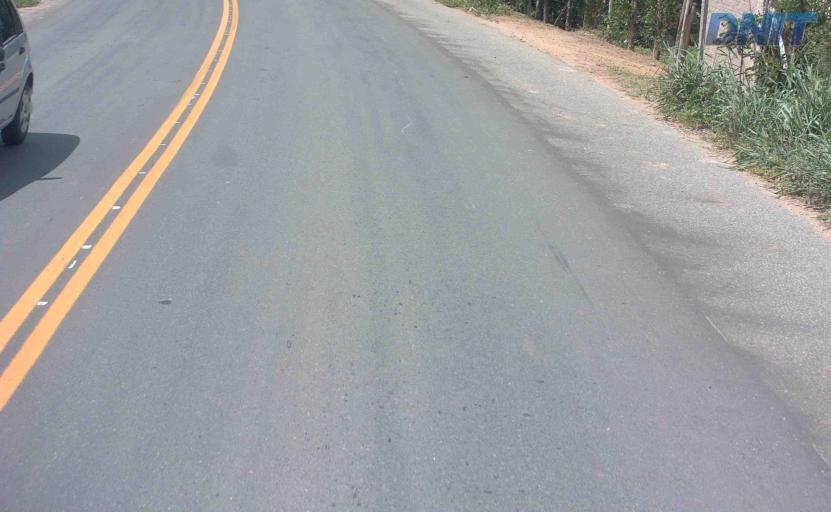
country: BR
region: Minas Gerais
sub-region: Governador Valadares
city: Governador Valadares
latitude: -18.9147
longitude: -42.0010
